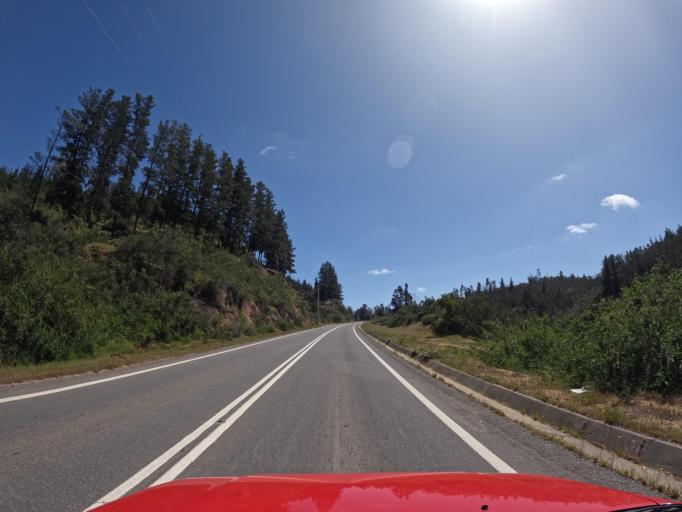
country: CL
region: O'Higgins
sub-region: Provincia de Colchagua
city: Santa Cruz
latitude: -34.6845
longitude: -71.7875
